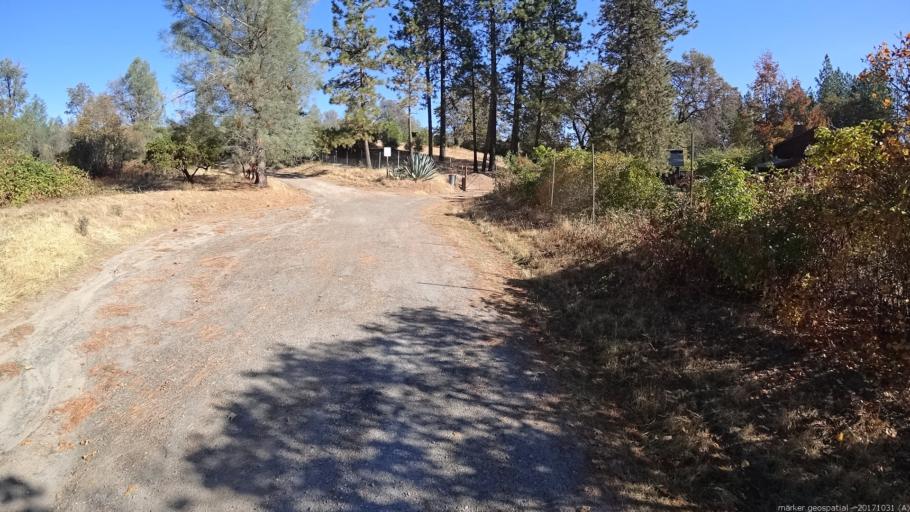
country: US
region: California
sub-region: Shasta County
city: Shingletown
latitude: 40.4470
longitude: -121.8330
